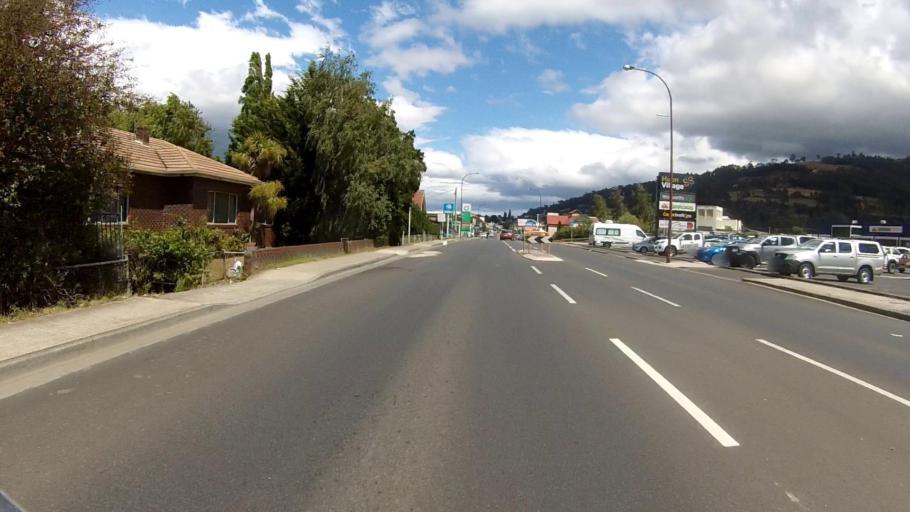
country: AU
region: Tasmania
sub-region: Huon Valley
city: Huonville
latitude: -43.0278
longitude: 147.0501
